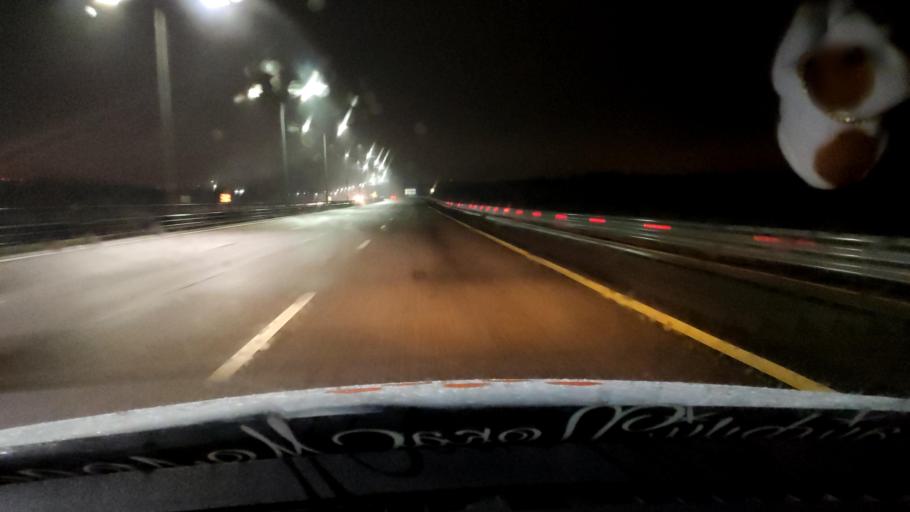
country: RU
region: Voronezj
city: Somovo
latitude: 51.7527
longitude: 39.3060
